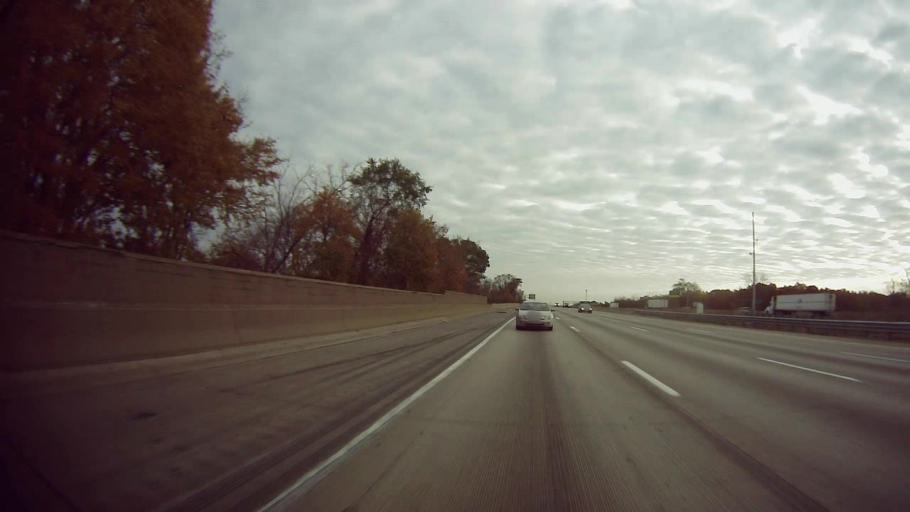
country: US
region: Michigan
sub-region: Wayne County
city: Romulus
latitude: 42.2257
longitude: -83.3970
